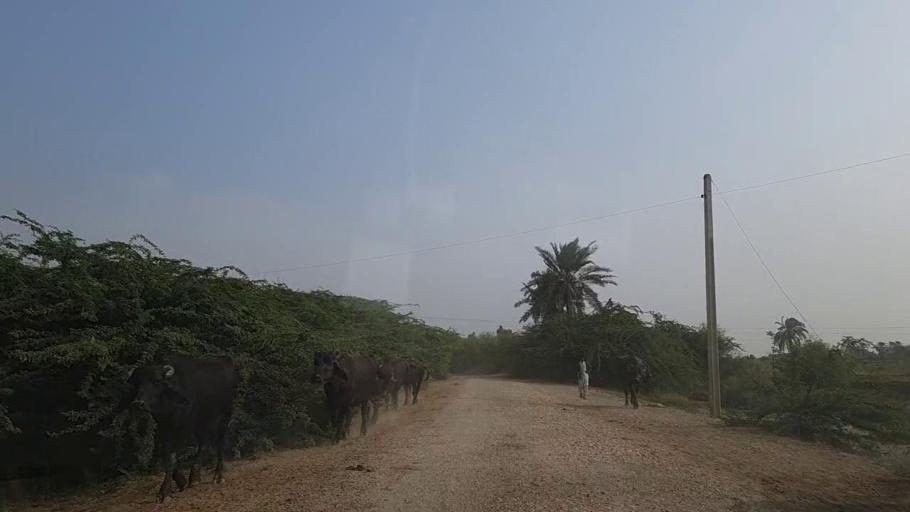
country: PK
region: Sindh
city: Gharo
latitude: 24.6525
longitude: 67.6204
